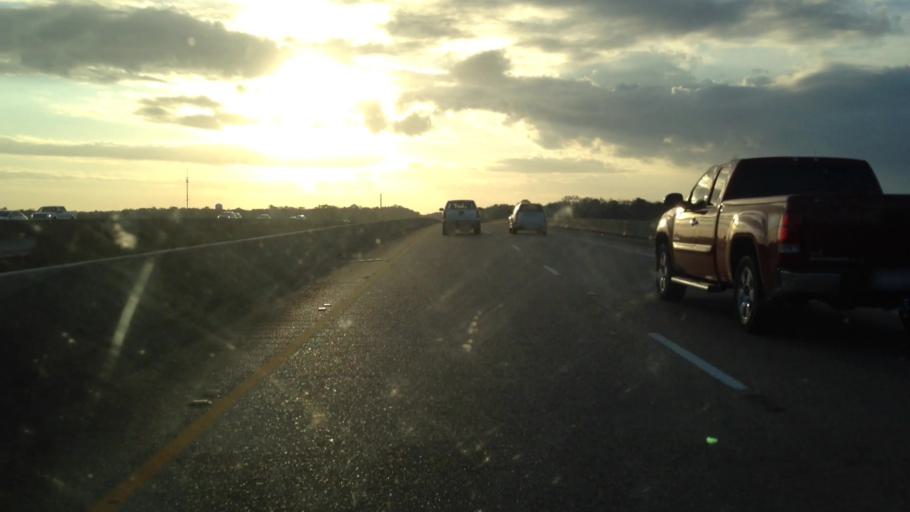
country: US
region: Mississippi
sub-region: Jackson County
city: Hickory Hills
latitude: 30.4381
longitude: -88.6099
